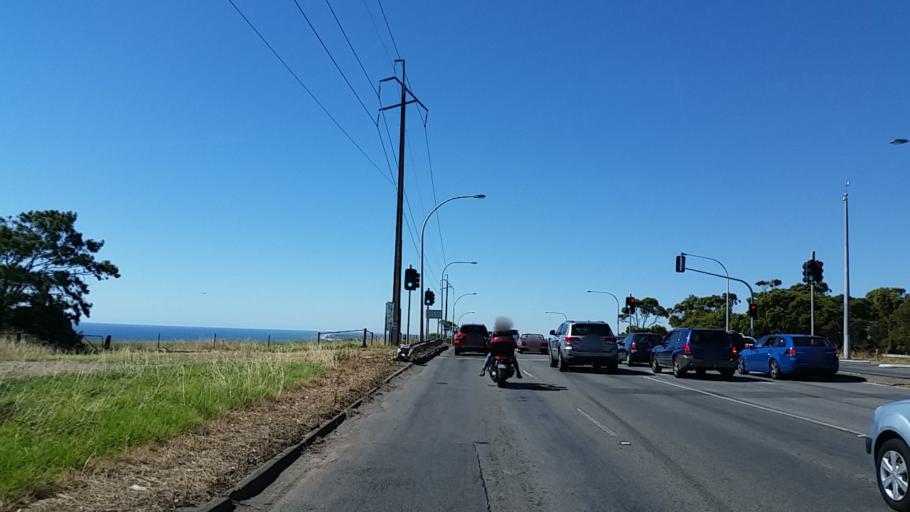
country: AU
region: South Australia
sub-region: Marion
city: Trott Park
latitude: -35.0554
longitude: 138.5350
